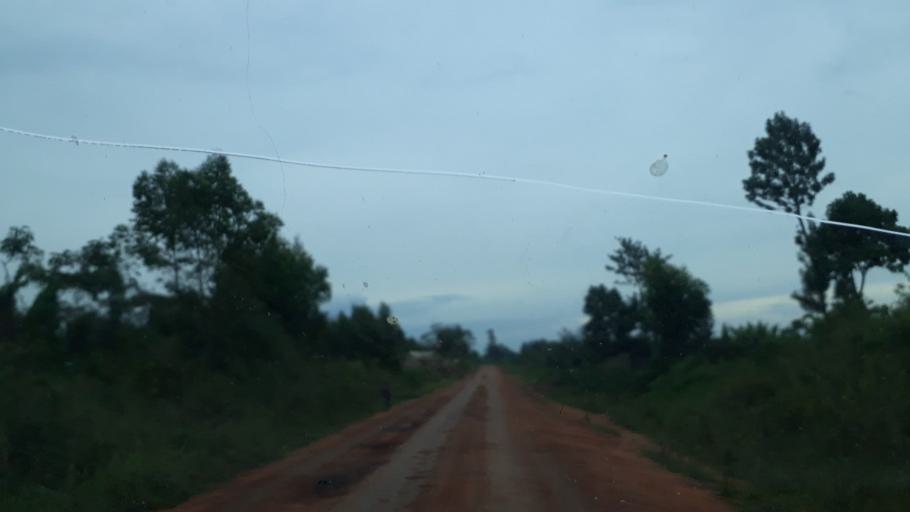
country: UG
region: Northern Region
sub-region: Zombo District
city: Paidha
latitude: 2.1831
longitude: 30.7227
